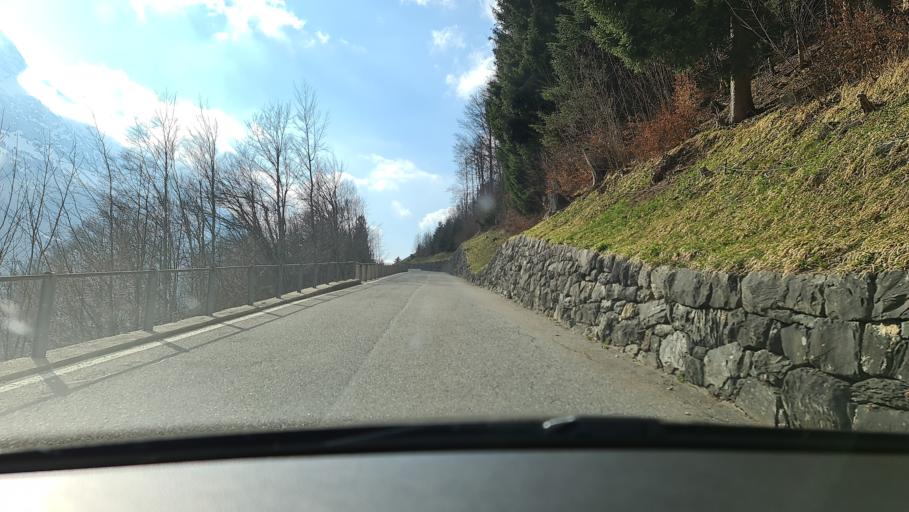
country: CH
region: Schwyz
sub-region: Bezirk Schwyz
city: Muotathal
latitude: 46.8663
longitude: 8.7776
